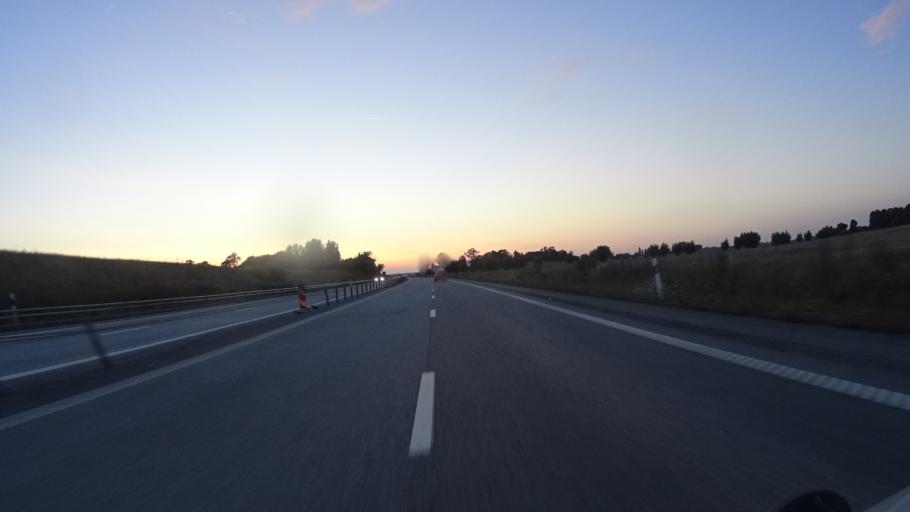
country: SE
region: Skane
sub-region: Vellinge Kommun
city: Vellinge
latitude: 55.4418
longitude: 13.0356
